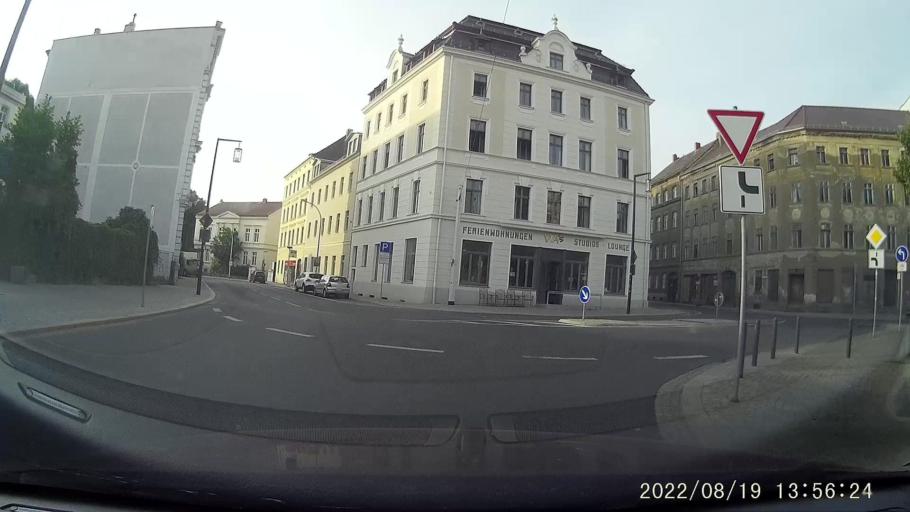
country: DE
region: Saxony
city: Goerlitz
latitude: 51.1550
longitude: 14.9637
